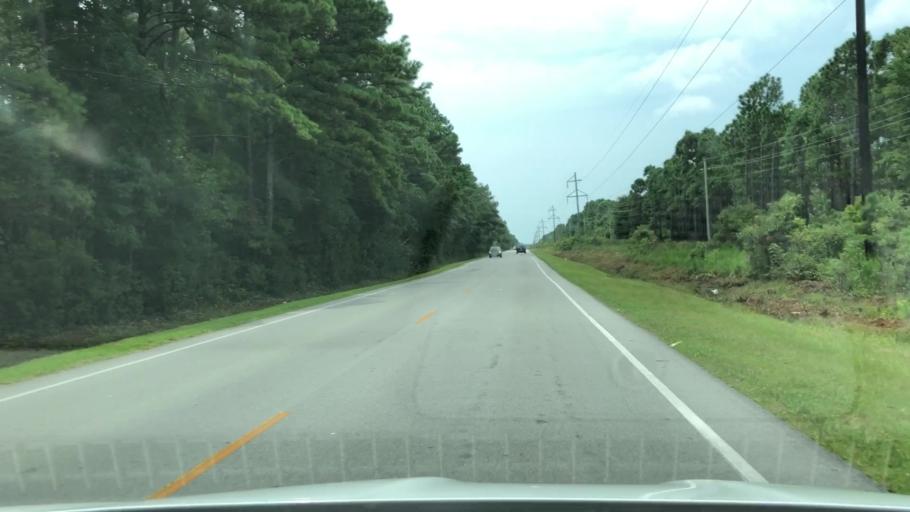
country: US
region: North Carolina
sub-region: Carteret County
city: Newport
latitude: 34.7600
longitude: -76.8718
